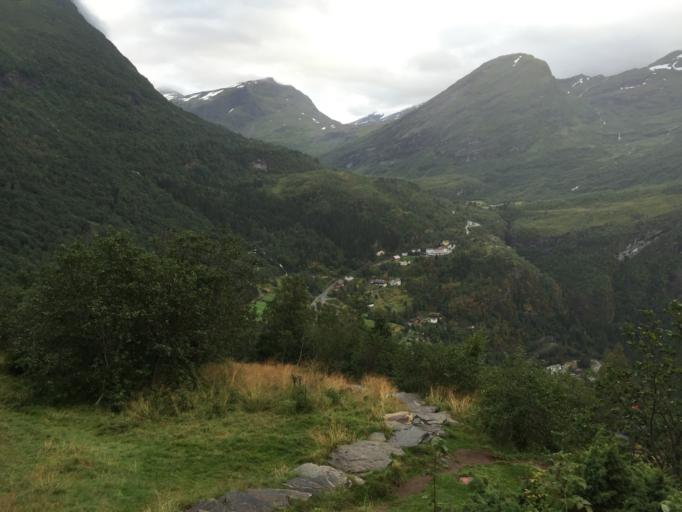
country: NO
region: More og Romsdal
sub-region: Norddal
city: Valldal
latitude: 62.1023
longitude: 7.2214
